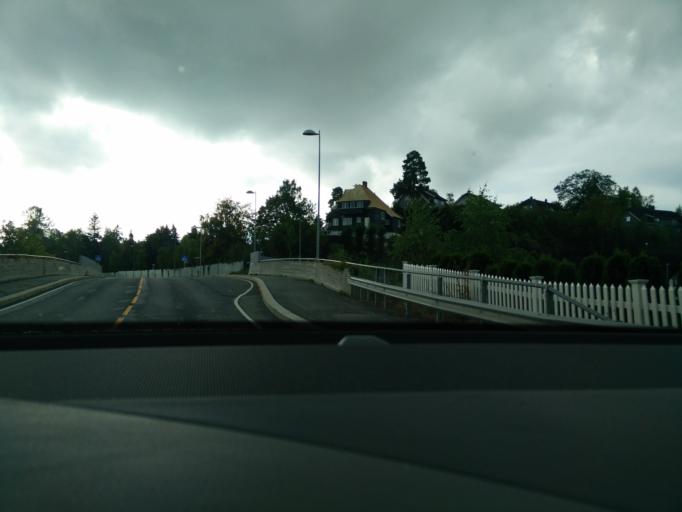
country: NO
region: Akershus
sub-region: Baerum
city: Lysaker
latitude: 59.9152
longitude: 10.6308
